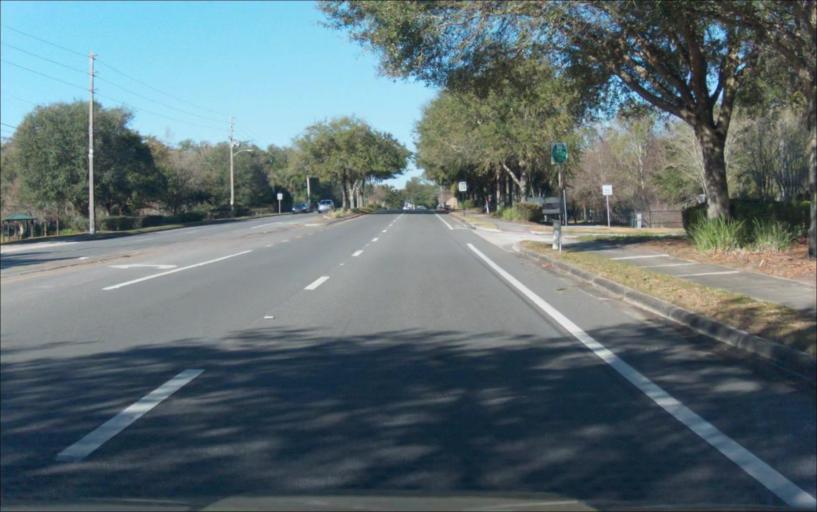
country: US
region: Florida
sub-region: Orange County
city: Maitland
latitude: 28.6337
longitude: -81.3722
